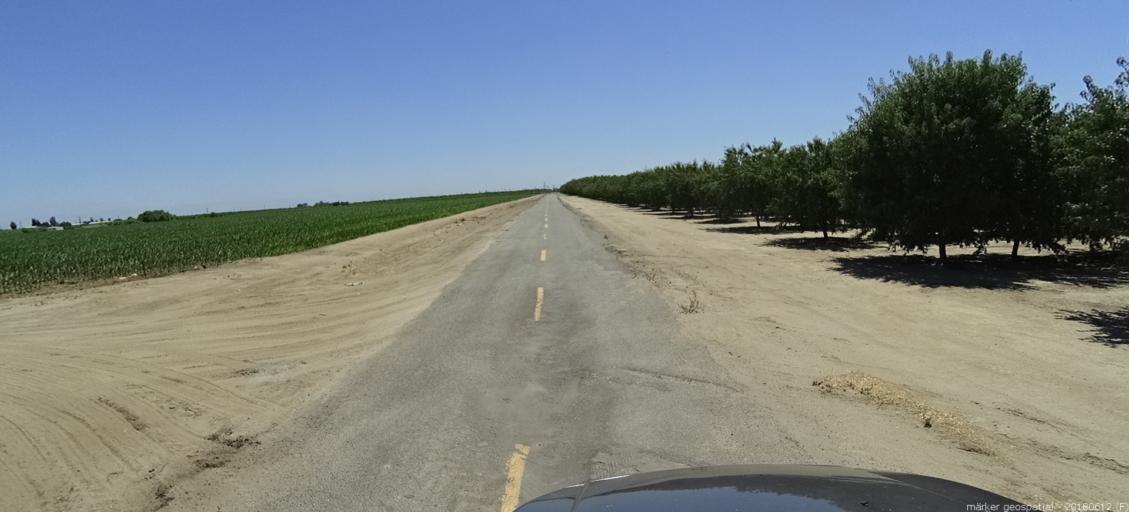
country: US
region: California
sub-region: Madera County
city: Chowchilla
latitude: 37.0616
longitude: -120.3403
